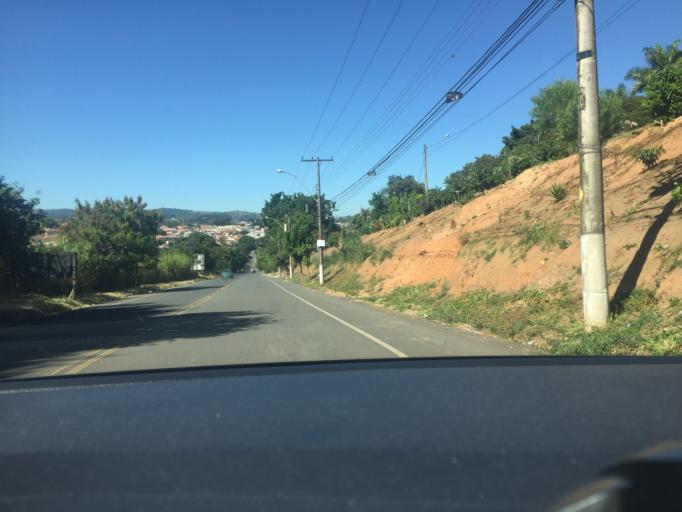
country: BR
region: Sao Paulo
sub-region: Santo Antonio Do Jardim
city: Espirito Santo do Pinhal
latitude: -22.1755
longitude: -46.7464
